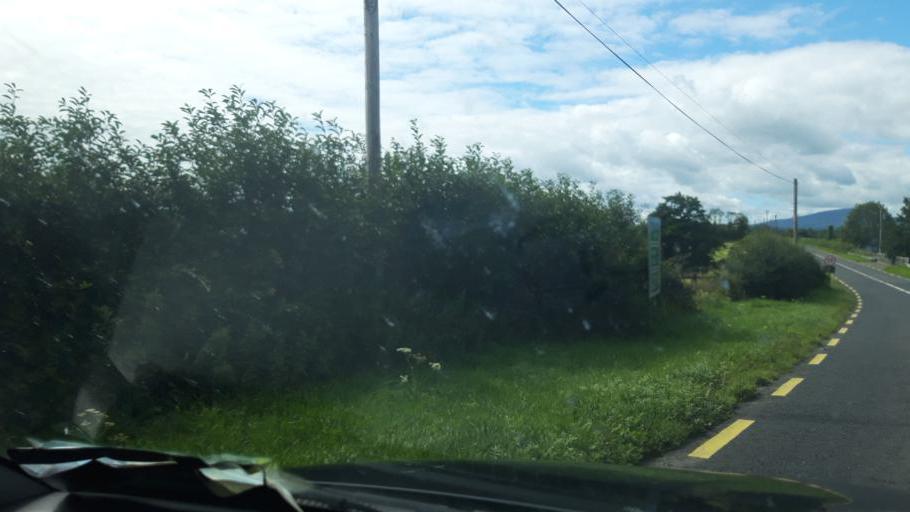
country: IE
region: Leinster
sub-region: Kilkenny
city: Callan
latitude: 52.5303
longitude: -7.4109
